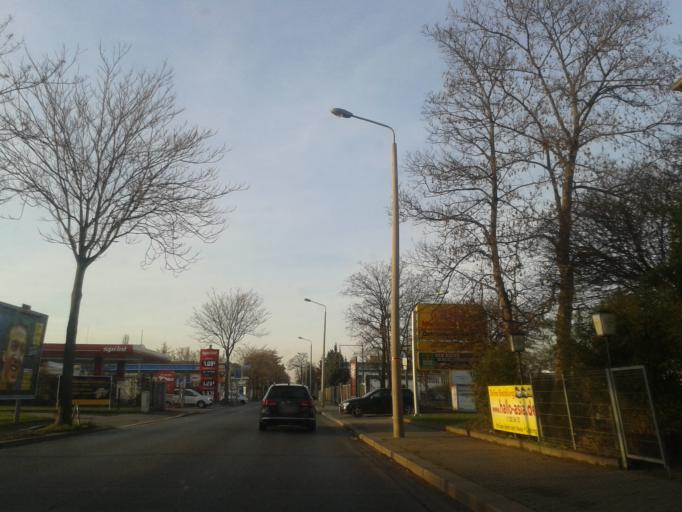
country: DE
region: Saxony
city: Heidenau
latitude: 51.0059
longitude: 13.8211
